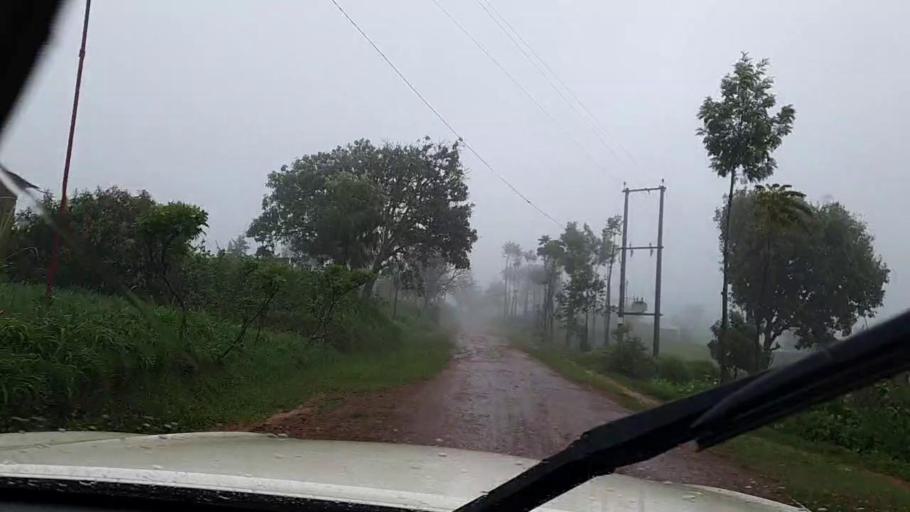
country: RW
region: Northern Province
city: Byumba
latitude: -1.7443
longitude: 30.0044
